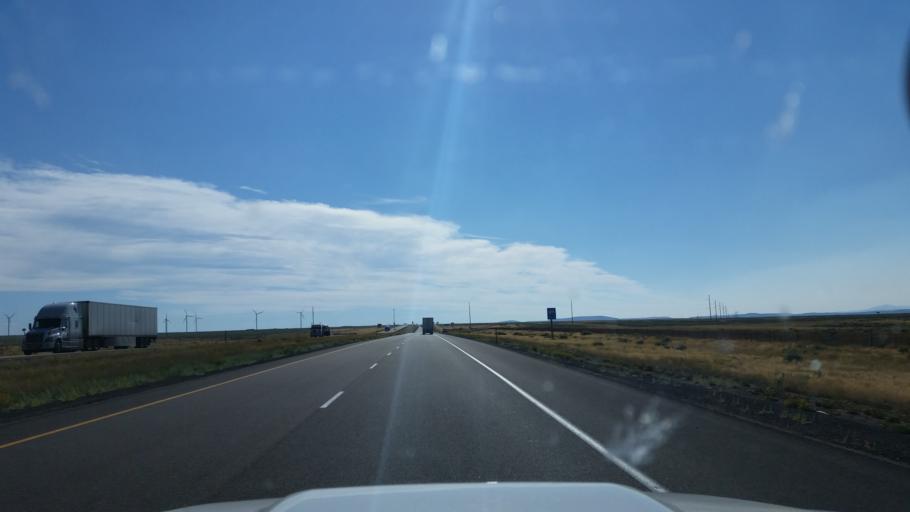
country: US
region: Wyoming
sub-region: Uinta County
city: Mountain View
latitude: 41.3096
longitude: -110.5186
